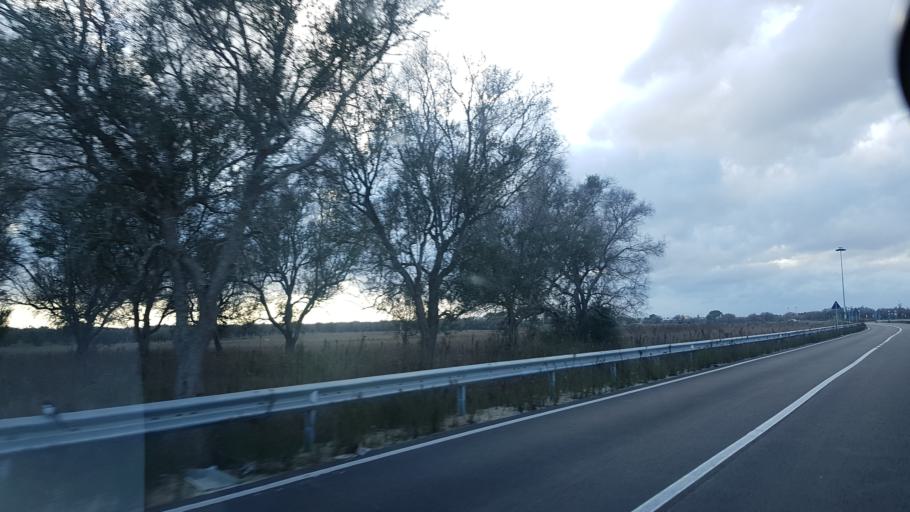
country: IT
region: Apulia
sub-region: Provincia di Brindisi
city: San Pietro Vernotico
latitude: 40.4872
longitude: 18.0239
